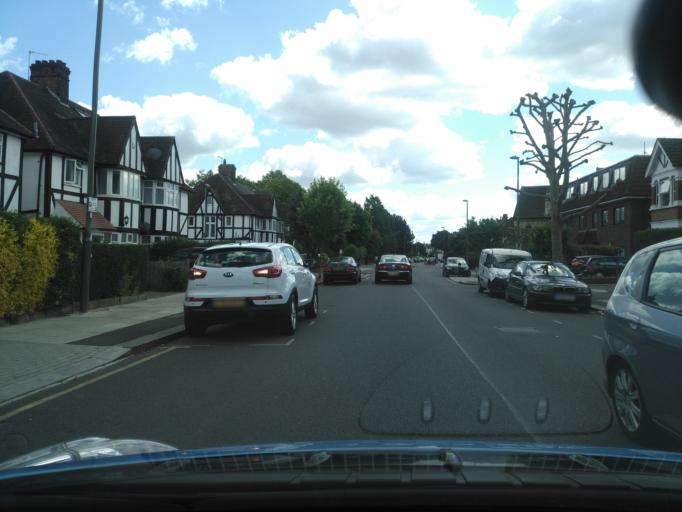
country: GB
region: England
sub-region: Greater London
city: Hendon
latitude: 51.6038
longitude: -0.1871
